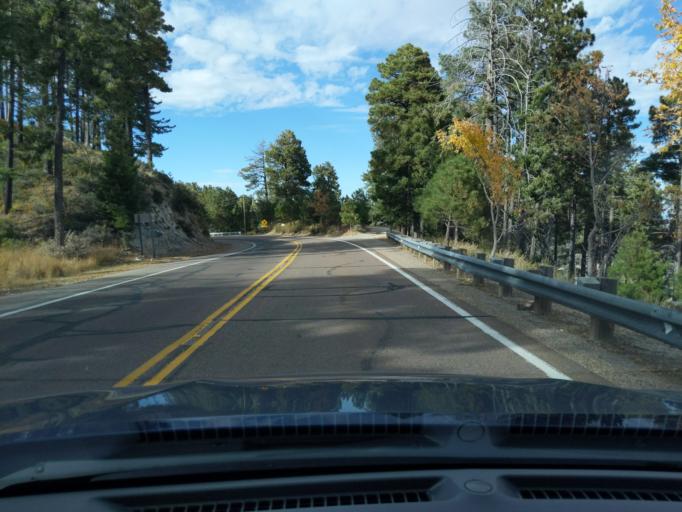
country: US
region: Arizona
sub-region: Pinal County
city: Oracle
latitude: 32.4467
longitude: -110.7534
